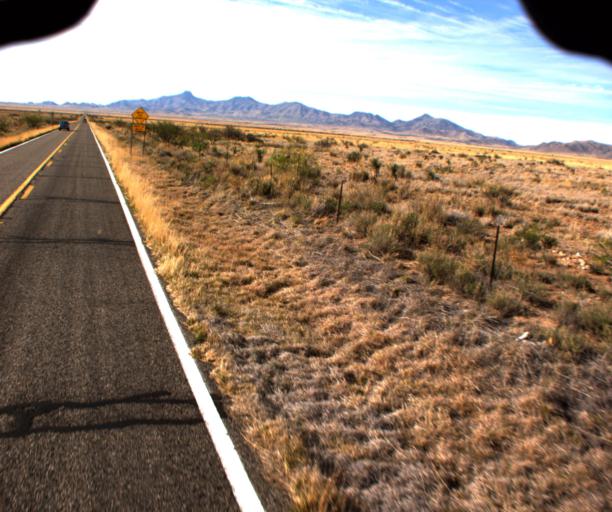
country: US
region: Arizona
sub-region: Cochise County
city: Willcox
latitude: 32.0367
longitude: -109.4776
